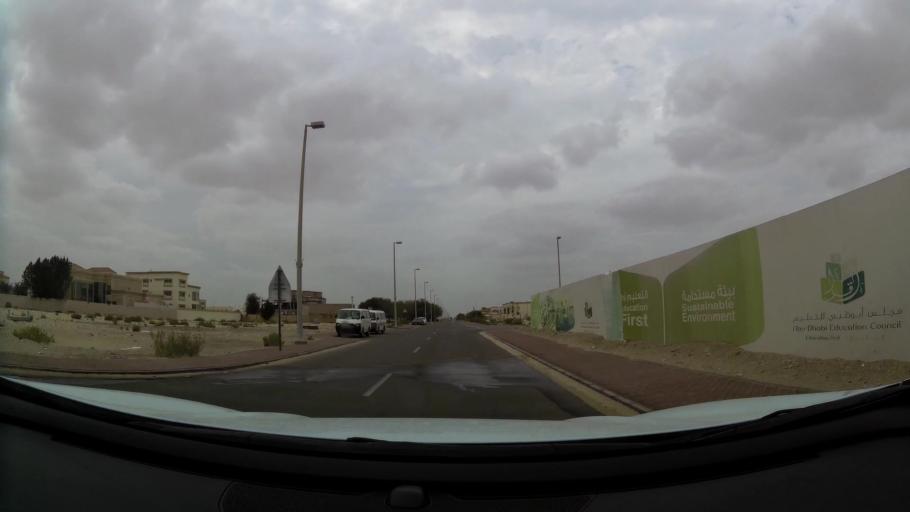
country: AE
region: Abu Dhabi
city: Abu Dhabi
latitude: 24.3709
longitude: 54.6383
